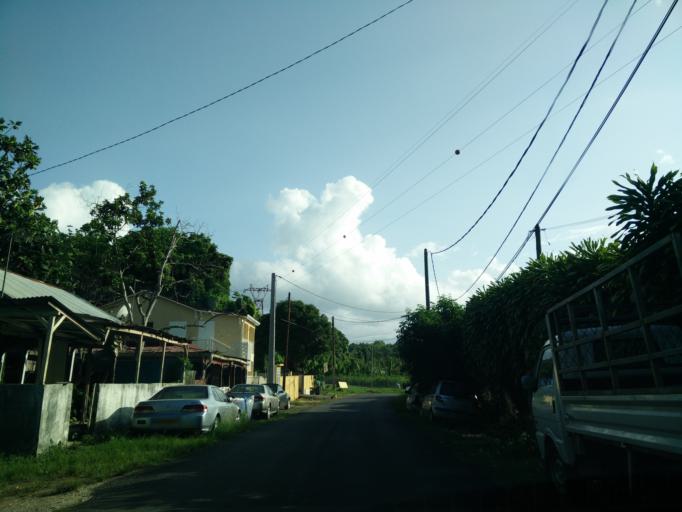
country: GP
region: Guadeloupe
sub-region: Guadeloupe
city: Pointe-a-Pitre
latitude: 16.2467
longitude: -61.5128
